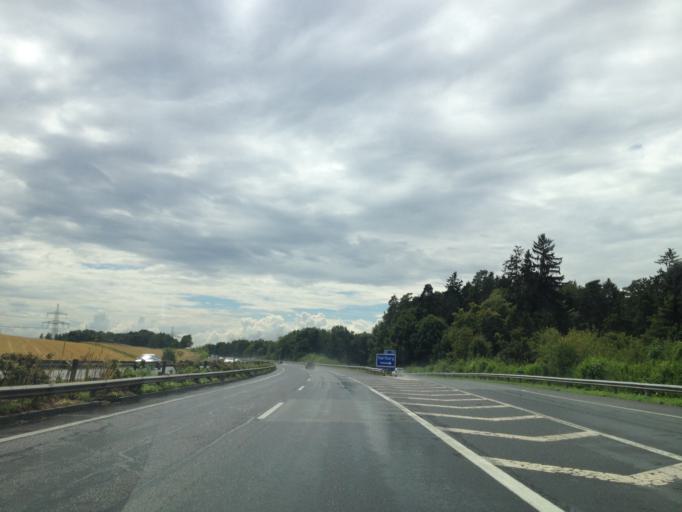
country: AT
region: Styria
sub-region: Politischer Bezirk Hartberg-Fuerstenfeld
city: Sankt Johann in der Haide
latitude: 47.2754
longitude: 16.0155
